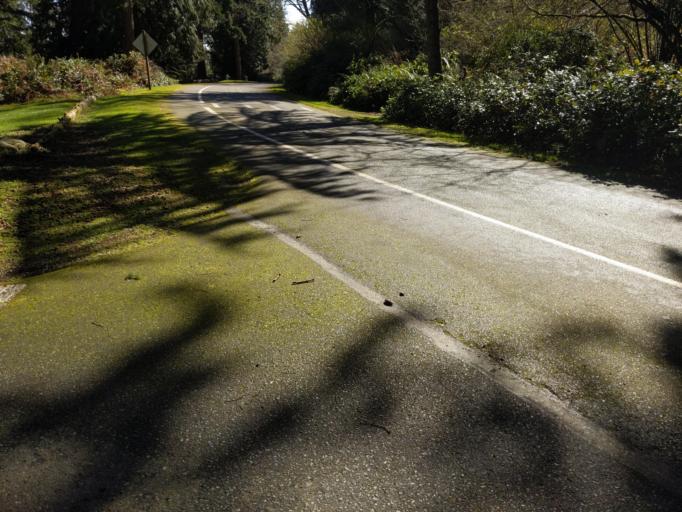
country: US
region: Washington
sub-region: Pierce County
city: Gig Harbor
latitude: 47.3165
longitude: -122.5353
